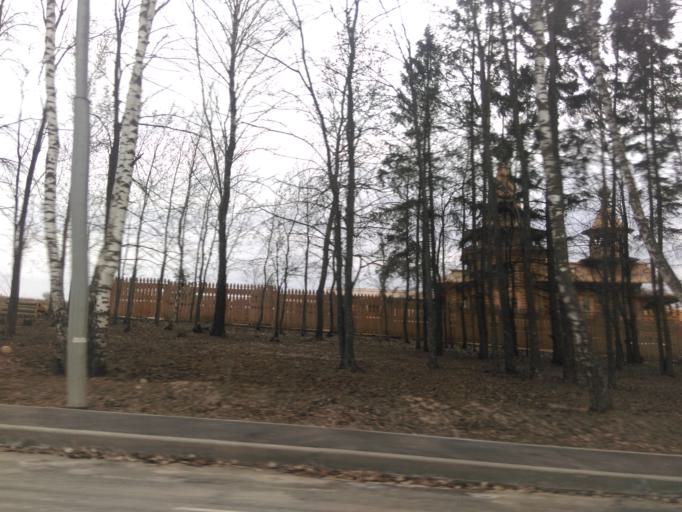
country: RU
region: Moskovskaya
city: Gorki Vtoryye
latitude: 55.7156
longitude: 37.1094
